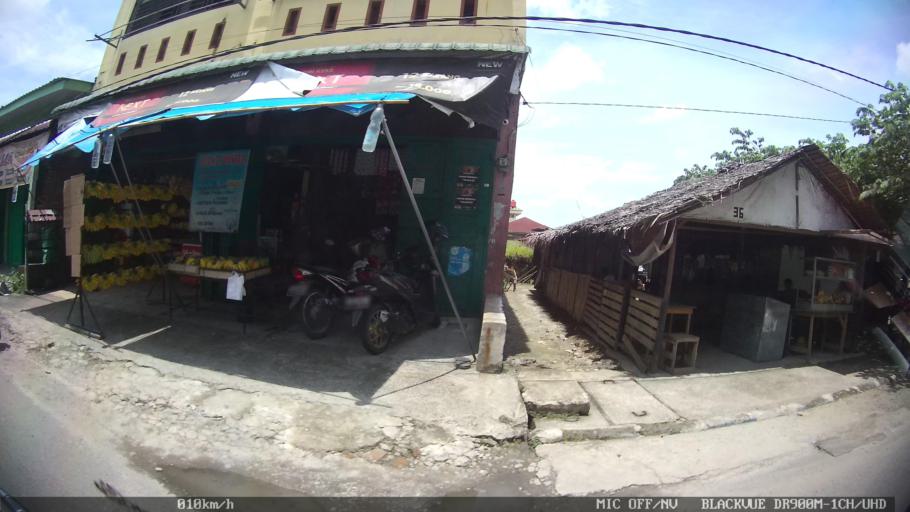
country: ID
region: North Sumatra
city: Percut
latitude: 3.5524
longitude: 98.8567
